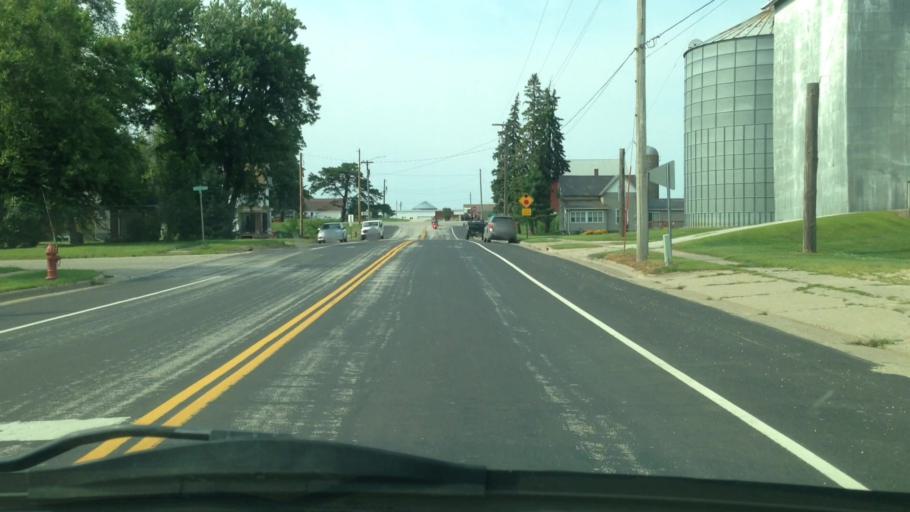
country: US
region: Minnesota
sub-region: Winona County
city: Lewiston
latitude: 43.9766
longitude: -91.9553
